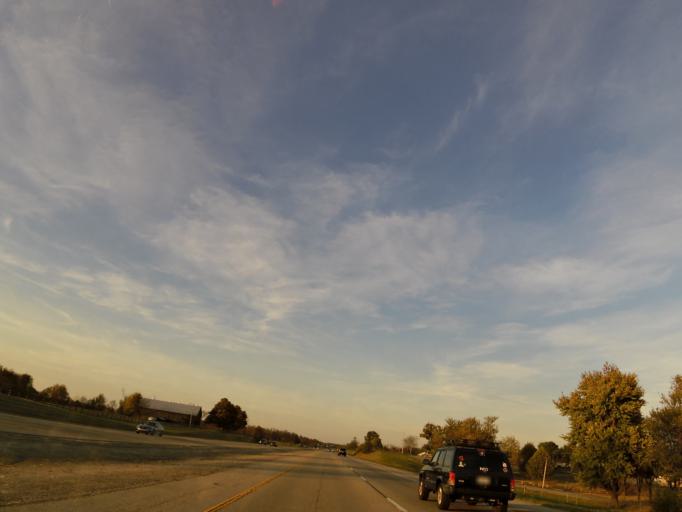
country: US
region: Kentucky
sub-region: Jessamine County
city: Nicholasville
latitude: 37.8086
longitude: -84.5999
